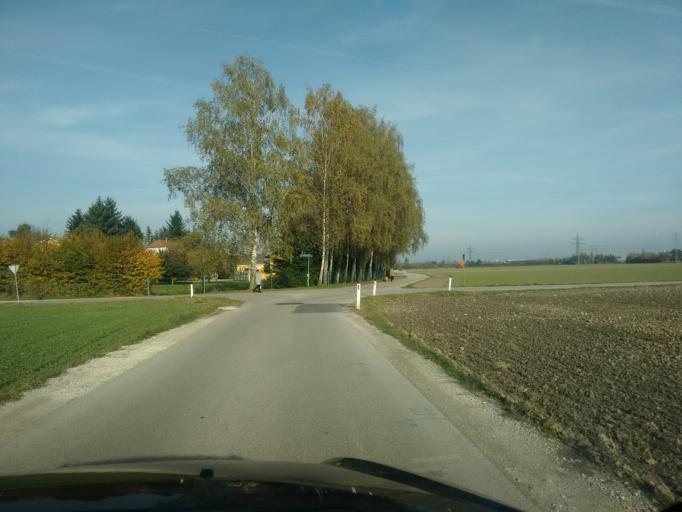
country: AT
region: Upper Austria
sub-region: Wels Stadt
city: Wels
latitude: 48.1813
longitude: 13.9927
